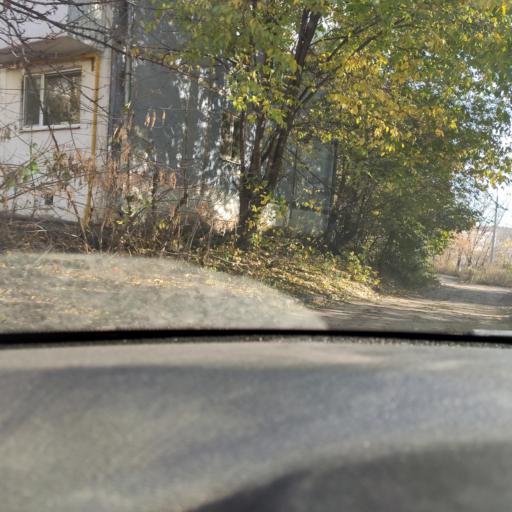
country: RU
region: Samara
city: Samara
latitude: 53.2470
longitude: 50.2214
